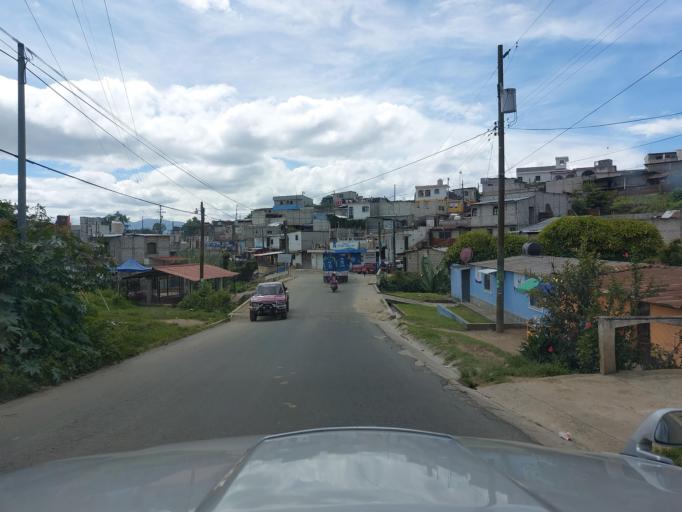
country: GT
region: Chimaltenango
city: San Andres Itzapa
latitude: 14.6206
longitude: -90.8365
